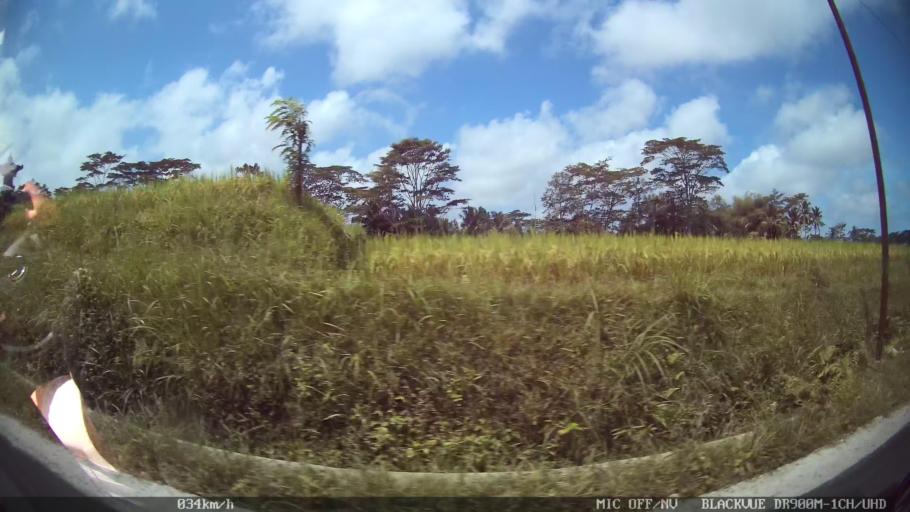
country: ID
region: Bali
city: Banjar Apuan Kaja
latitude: -8.4950
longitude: 115.3415
